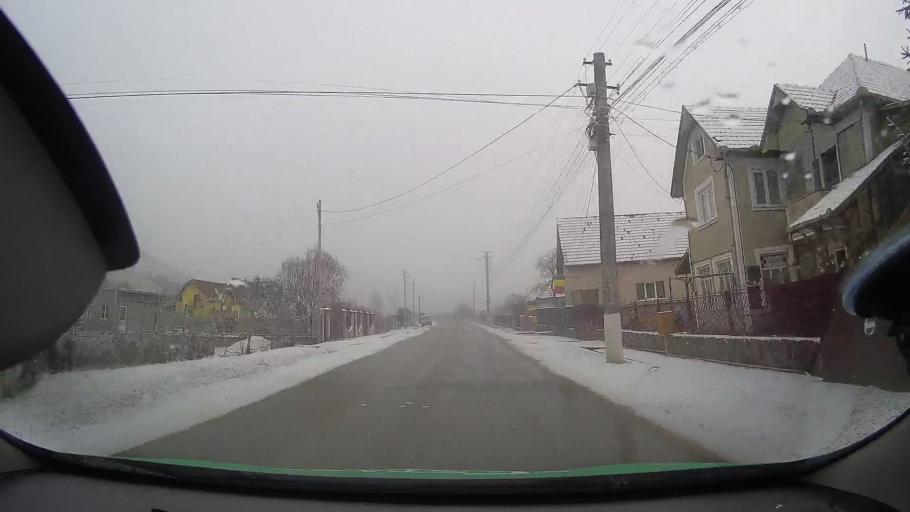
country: RO
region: Alba
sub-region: Municipiul Aiud
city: Ciumbrud
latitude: 46.3104
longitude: 23.7733
